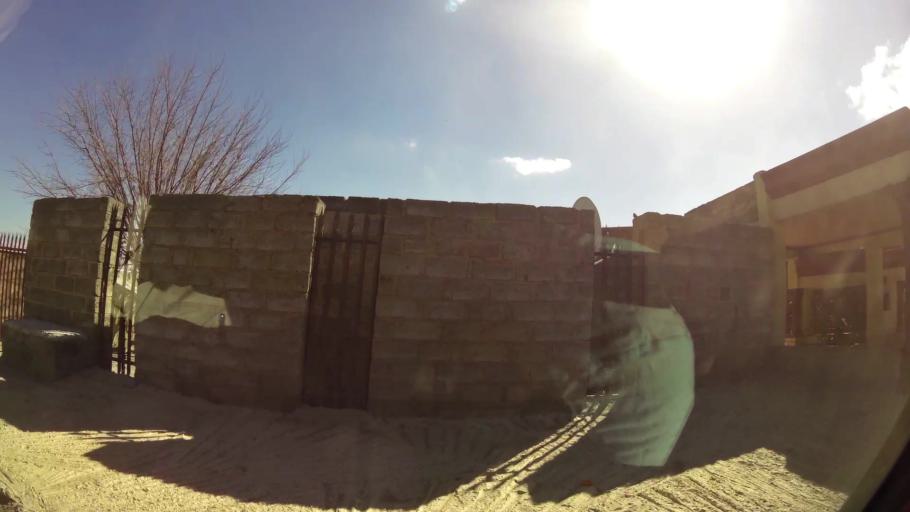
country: ZA
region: Gauteng
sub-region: City of Johannesburg Metropolitan Municipality
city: Midrand
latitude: -26.0324
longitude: 28.1574
